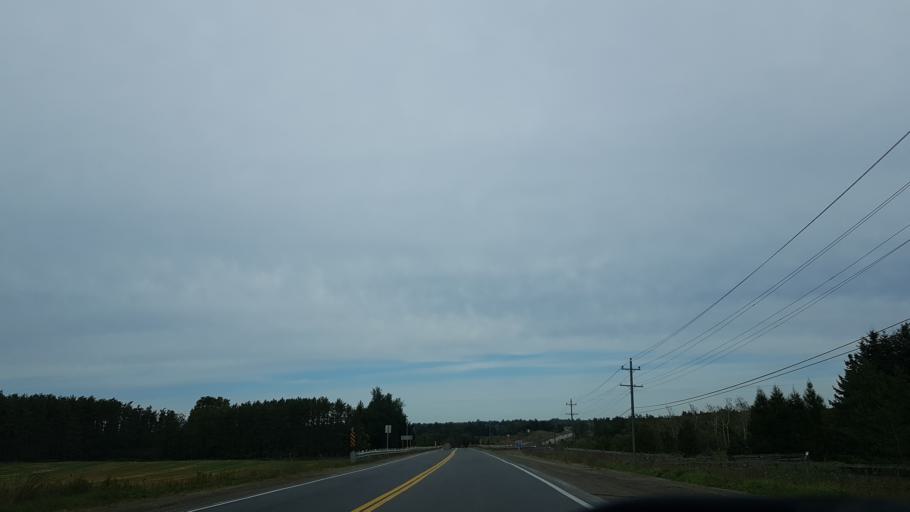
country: CA
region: Ontario
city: Orangeville
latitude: 43.8343
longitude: -80.0269
